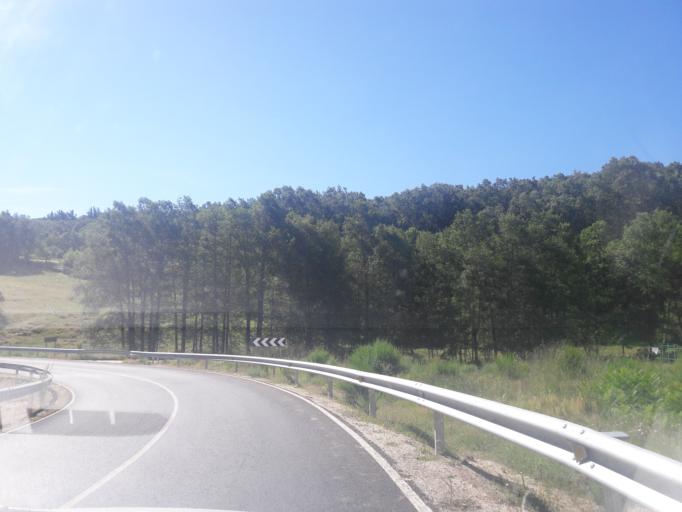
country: ES
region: Castille and Leon
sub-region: Provincia de Salamanca
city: Penacaballera
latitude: 40.3414
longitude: -5.8747
